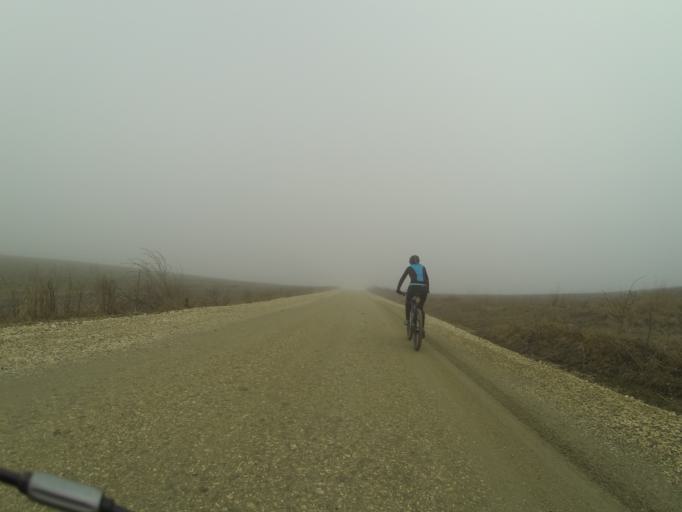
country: RO
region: Mehedinti
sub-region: Comuna Balacita
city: Gvardinita
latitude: 44.4277
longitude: 23.1308
